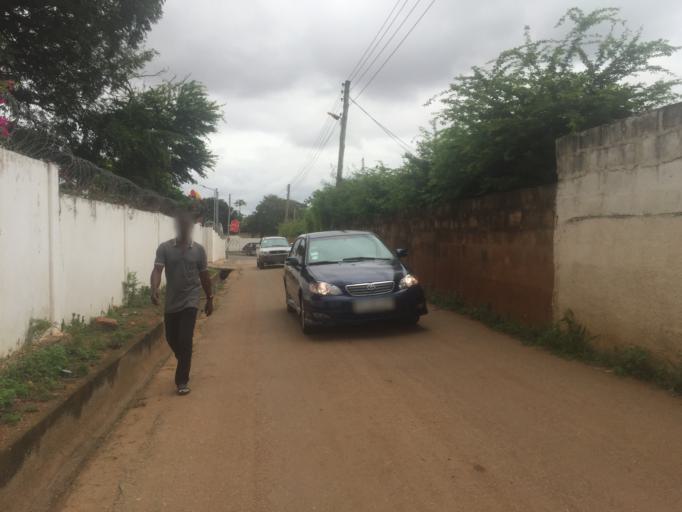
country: GH
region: Greater Accra
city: Accra
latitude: 5.5988
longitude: -0.2246
